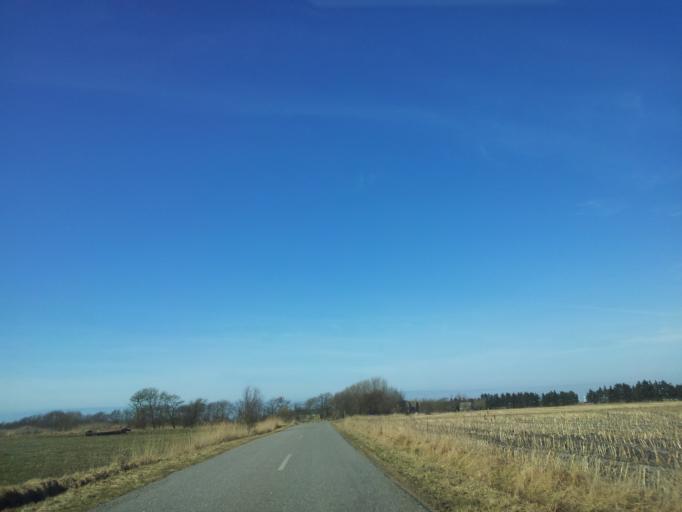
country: DK
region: South Denmark
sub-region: Tonder Kommune
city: Sherrebek
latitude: 55.1766
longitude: 8.7201
